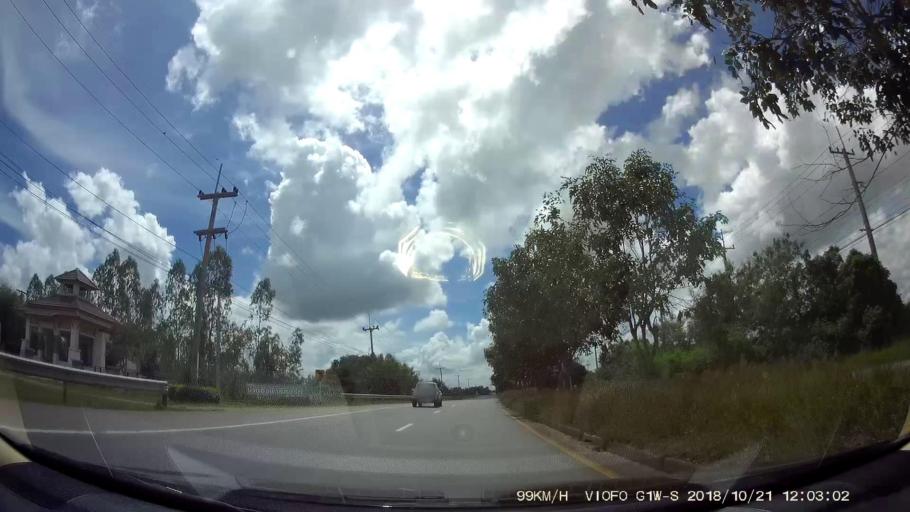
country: TH
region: Chaiyaphum
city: Chatturat
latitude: 15.5155
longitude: 101.8247
